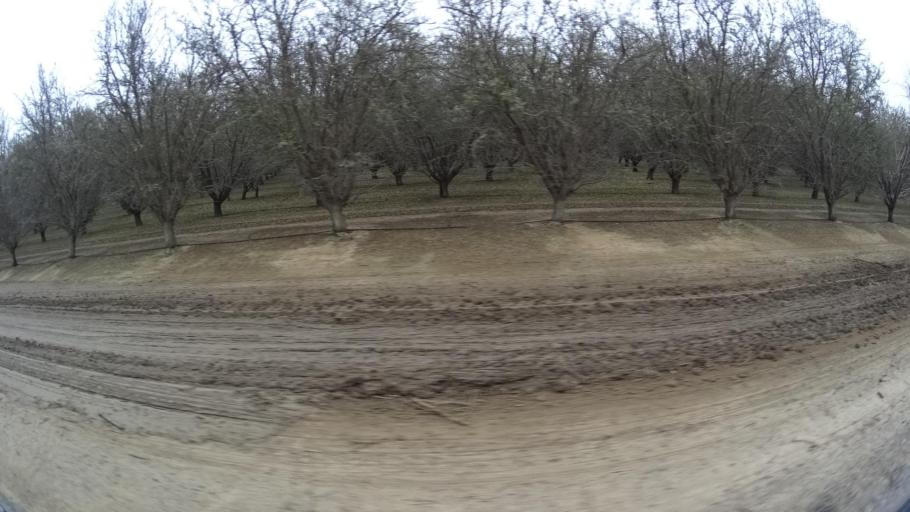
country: US
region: California
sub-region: Kern County
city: Wasco
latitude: 35.5813
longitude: -119.5094
